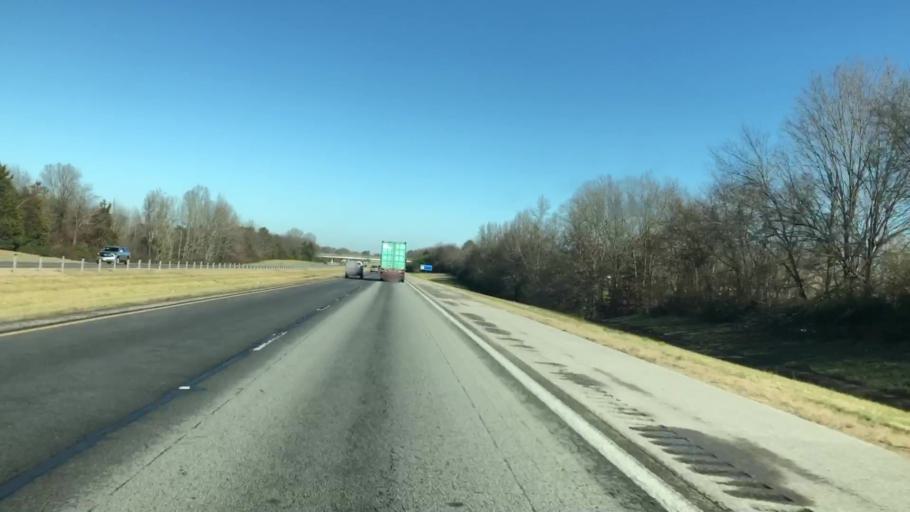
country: US
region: Alabama
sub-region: Limestone County
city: Athens
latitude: 34.8058
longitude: -86.9386
